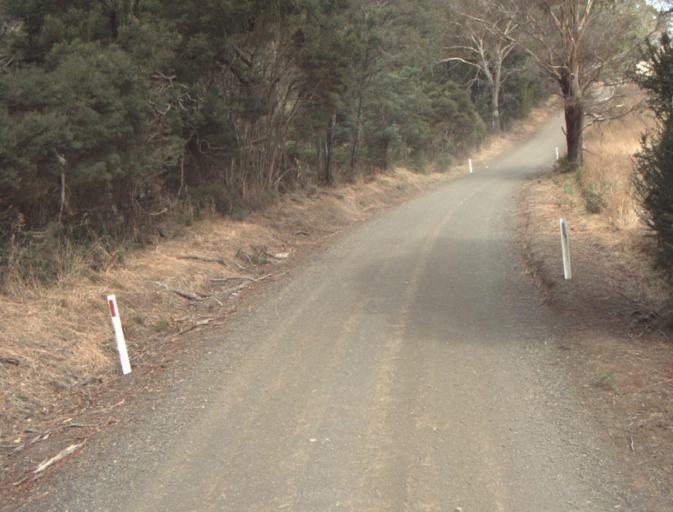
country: AU
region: Tasmania
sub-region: Launceston
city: Mayfield
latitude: -41.3014
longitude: 146.9940
